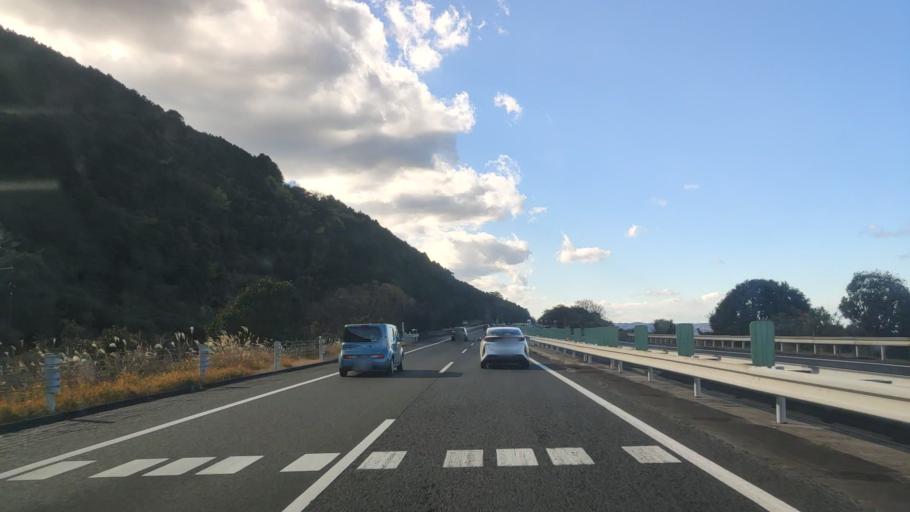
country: JP
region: Ehime
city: Kawanoecho
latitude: 33.9615
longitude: 133.5139
